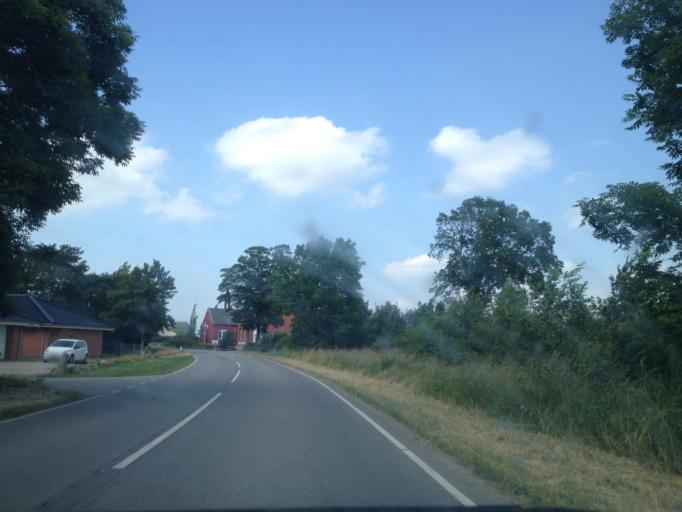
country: DK
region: South Denmark
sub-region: Kolding Kommune
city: Vamdrup
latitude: 55.3769
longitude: 9.2778
